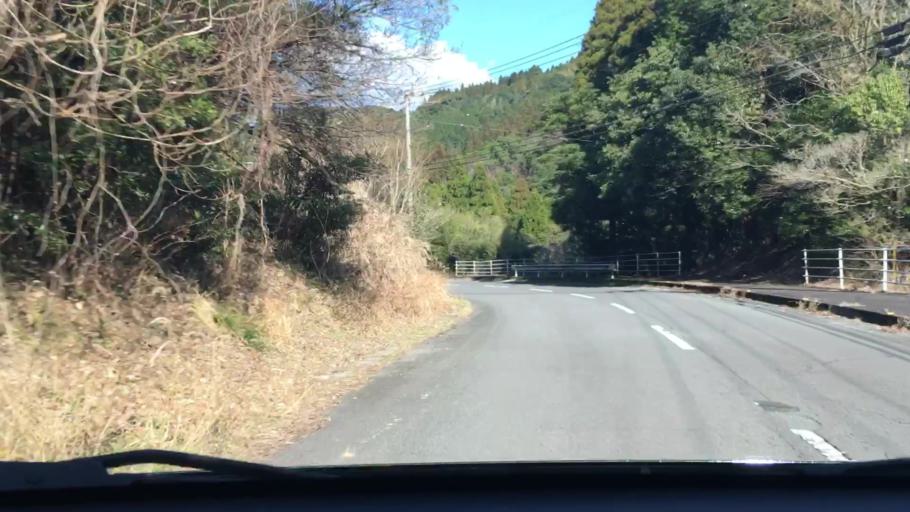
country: JP
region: Kagoshima
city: Satsumasendai
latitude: 31.7469
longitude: 130.4098
